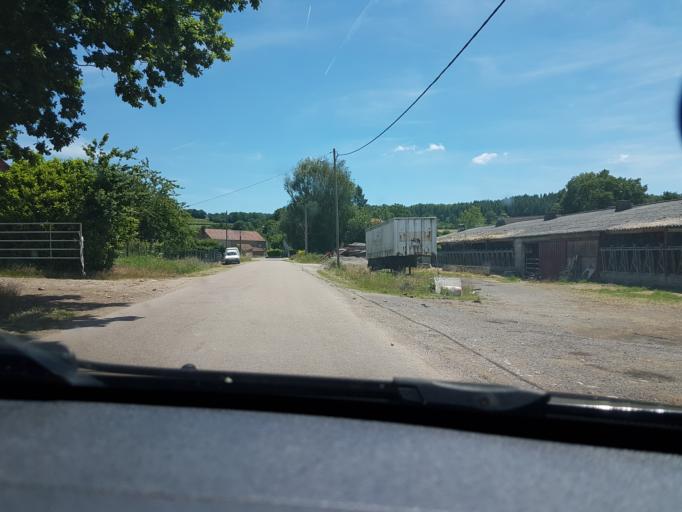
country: FR
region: Bourgogne
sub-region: Departement de Saone-et-Loire
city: Epinac
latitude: 46.9742
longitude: 4.5055
